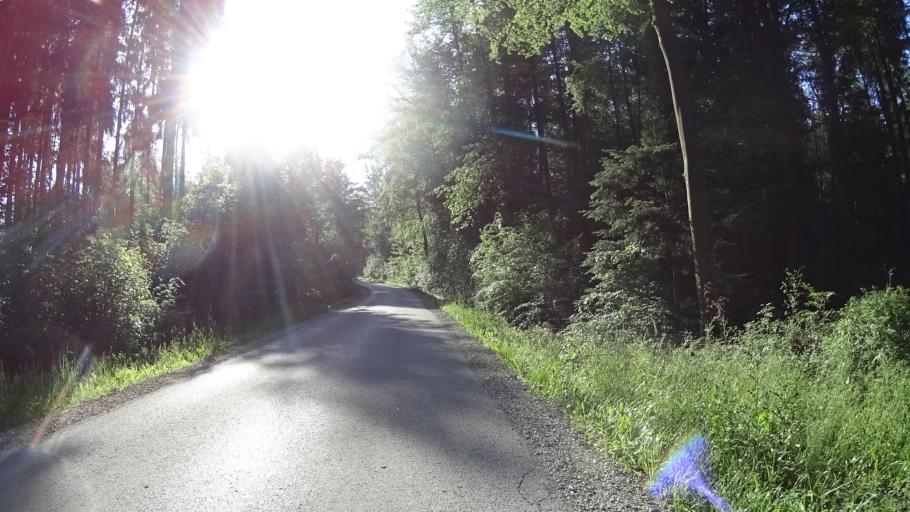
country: DE
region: Bavaria
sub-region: Regierungsbezirk Mittelfranken
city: Lichtenau
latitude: 49.1505
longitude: 10.4001
